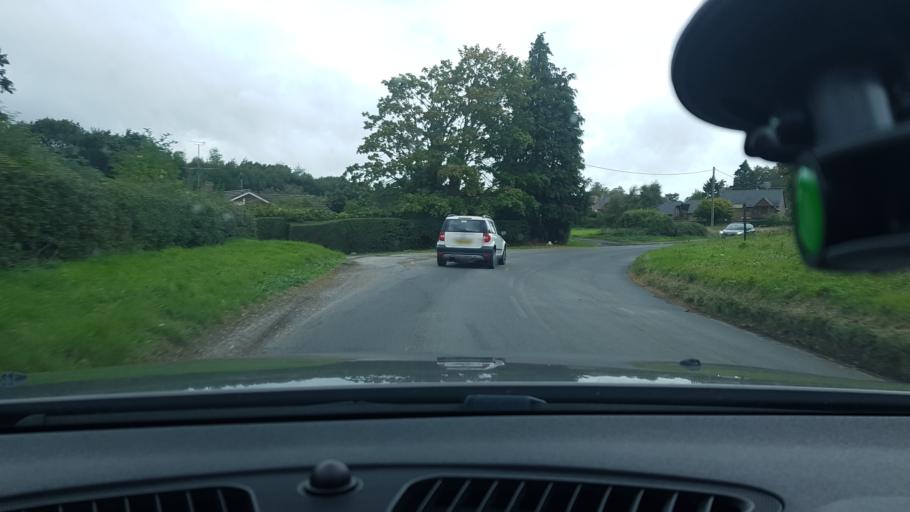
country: GB
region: England
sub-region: Wiltshire
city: Great Bedwyn
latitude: 51.3434
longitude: -1.6252
